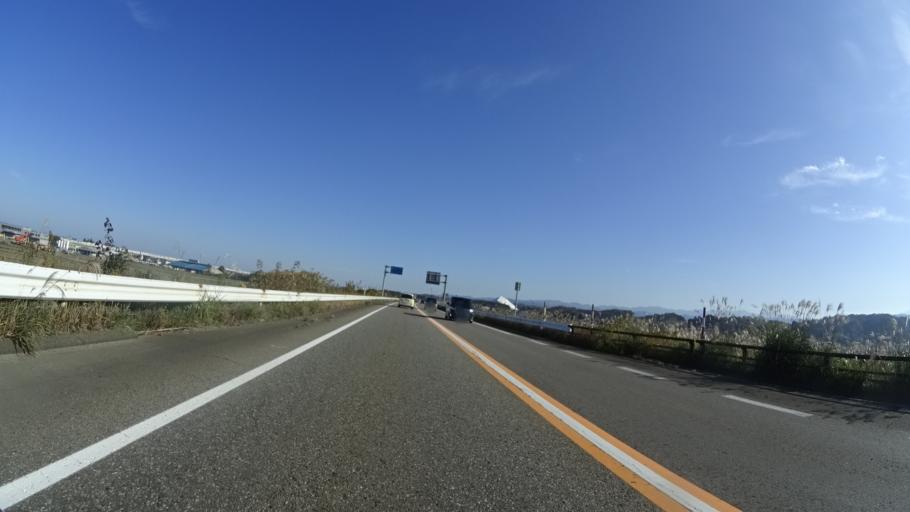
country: JP
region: Ishikawa
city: Komatsu
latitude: 36.3301
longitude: 136.4168
